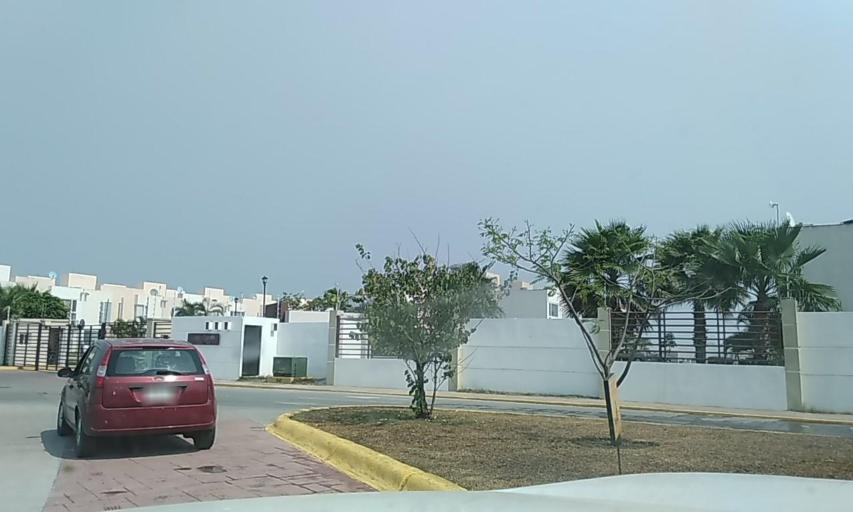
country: MX
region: Veracruz
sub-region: Veracruz
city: Hacienda Sotavento
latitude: 19.1327
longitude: -96.1675
